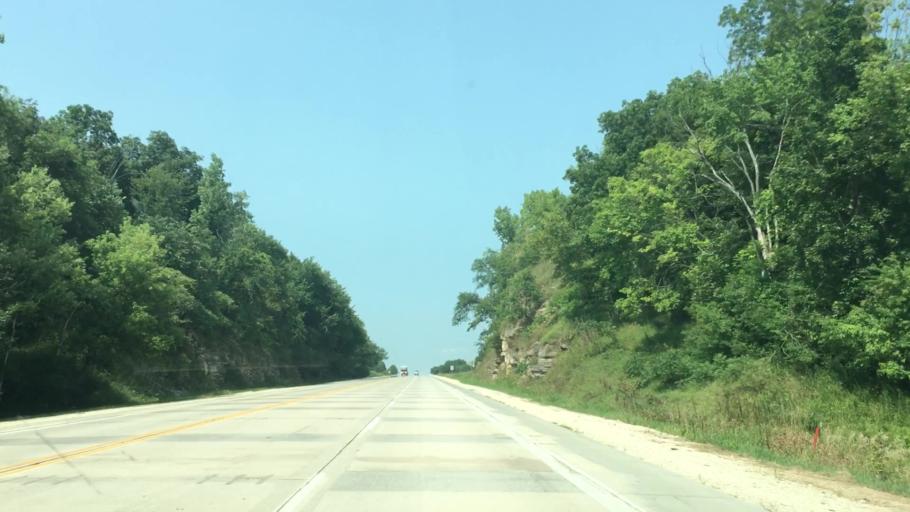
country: US
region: Iowa
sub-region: Winneshiek County
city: Decorah
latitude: 43.3250
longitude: -91.8134
